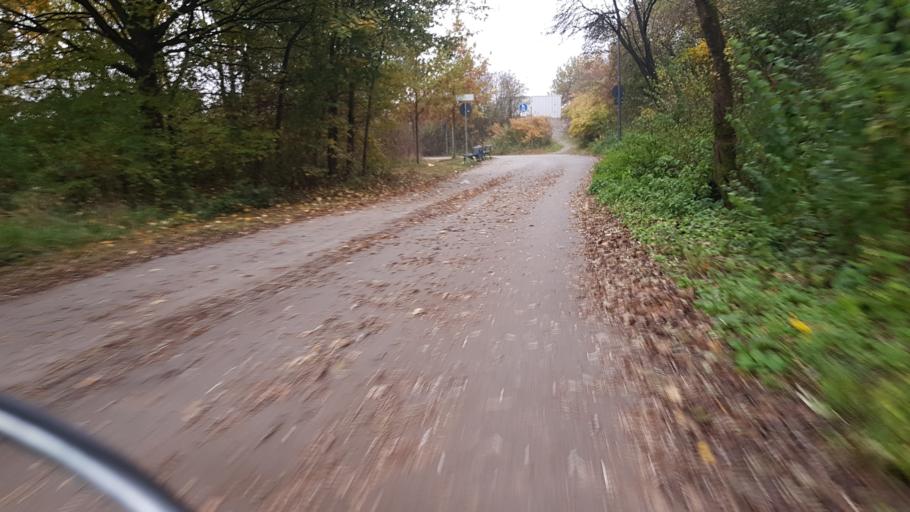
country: DE
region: Bavaria
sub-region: Upper Bavaria
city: Pasing
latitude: 48.1497
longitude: 11.4872
